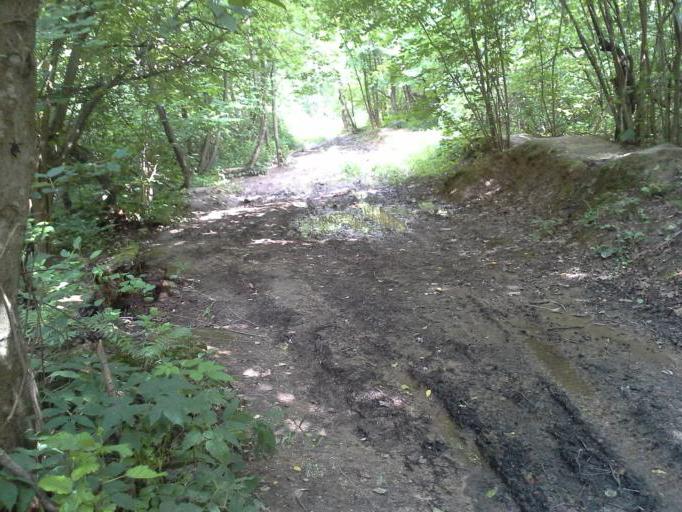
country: RU
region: Moskovskaya
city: Moskovskiy
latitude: 55.5887
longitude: 37.3857
